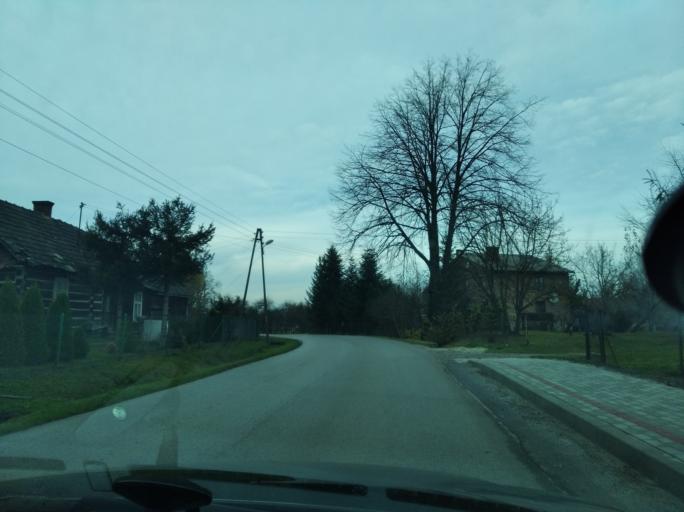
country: PL
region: Subcarpathian Voivodeship
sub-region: Powiat przeworski
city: Grzeska
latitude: 50.0885
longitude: 22.4462
